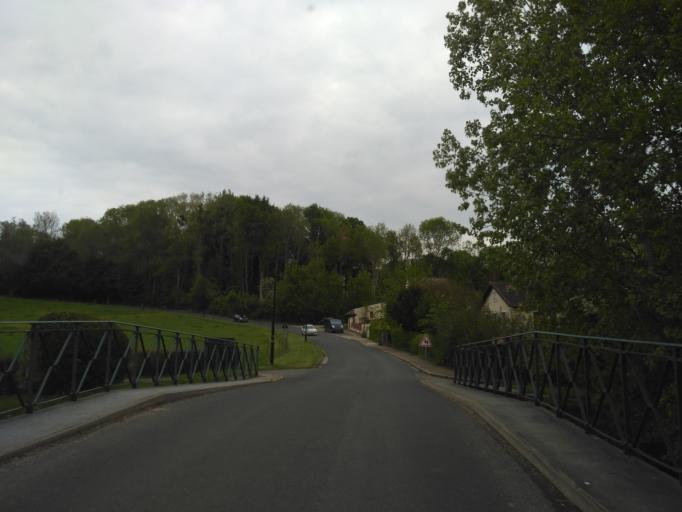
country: FR
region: Ile-de-France
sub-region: Departement de Seine-et-Marne
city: Moisenay
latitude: 48.5709
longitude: 2.7823
